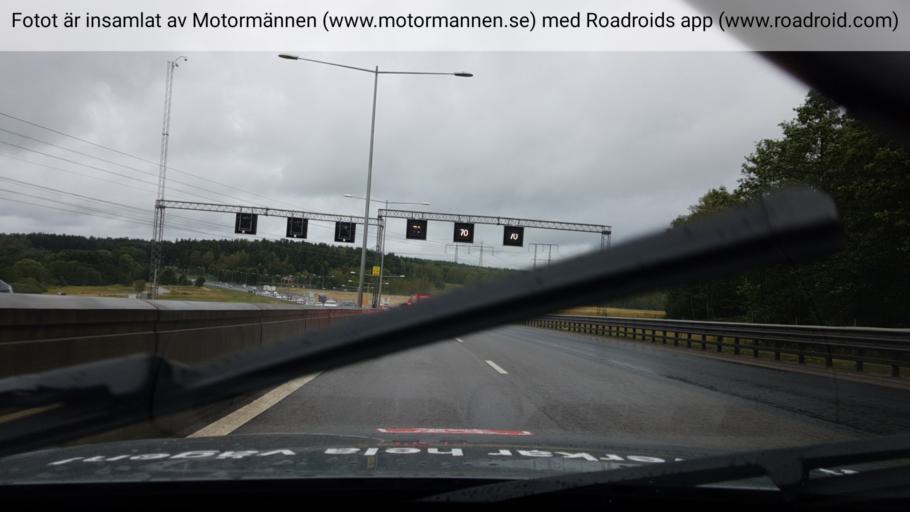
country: SE
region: Stockholm
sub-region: Salems Kommun
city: Ronninge
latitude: 59.2132
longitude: 17.7717
